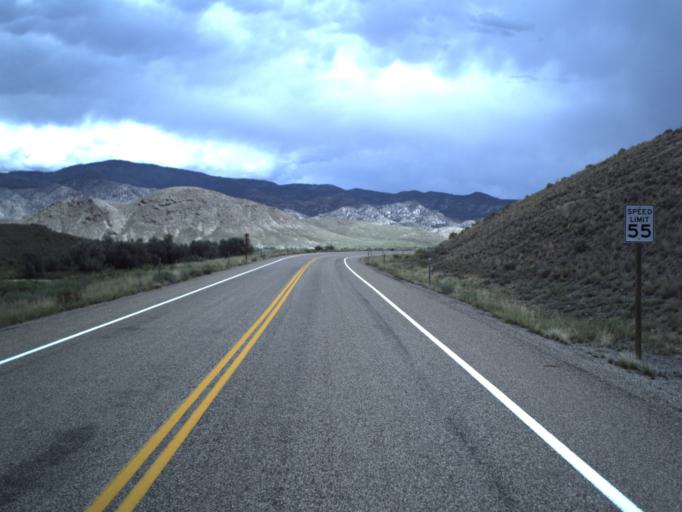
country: US
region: Utah
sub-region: Piute County
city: Junction
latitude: 38.2099
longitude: -112.2211
